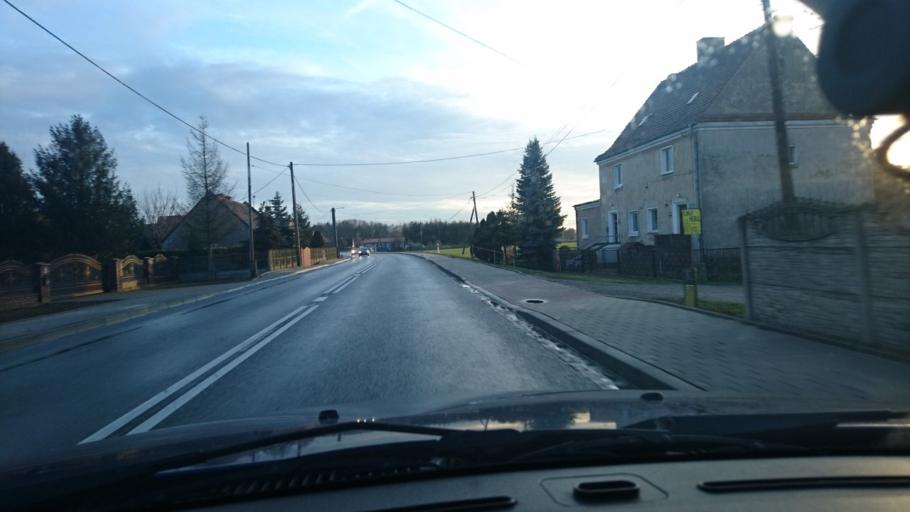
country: PL
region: Greater Poland Voivodeship
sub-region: Powiat kepinski
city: Opatow
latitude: 51.1690
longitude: 18.1466
